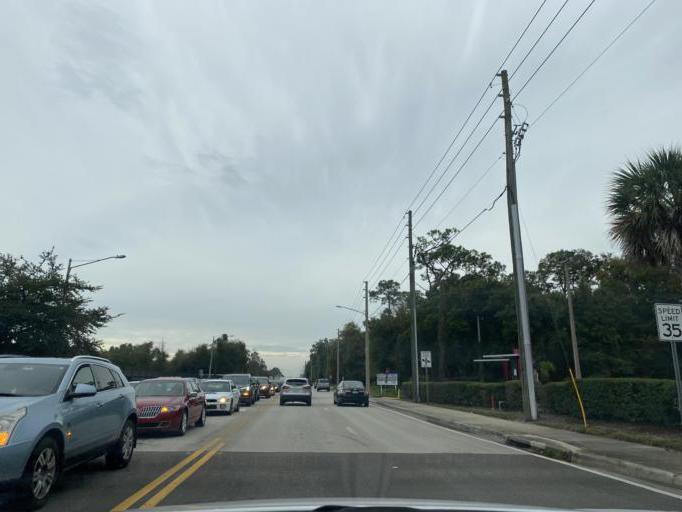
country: US
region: Florida
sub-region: Orange County
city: Winter Garden
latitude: 28.5507
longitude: -81.5835
